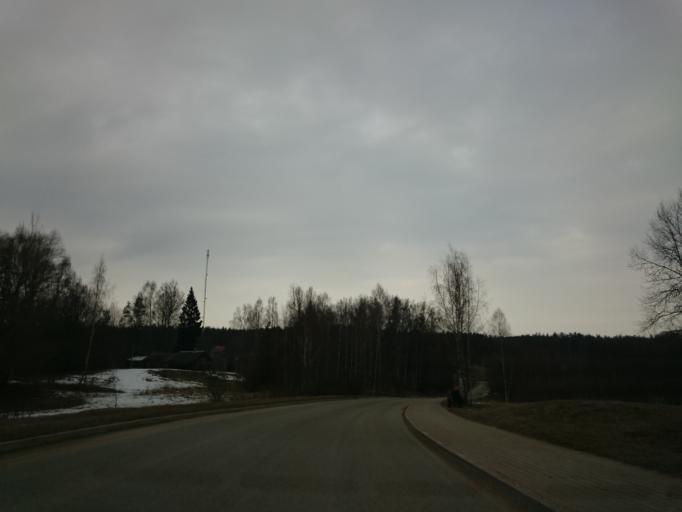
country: LV
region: Cesu Rajons
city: Cesis
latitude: 57.3195
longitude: 25.2568
